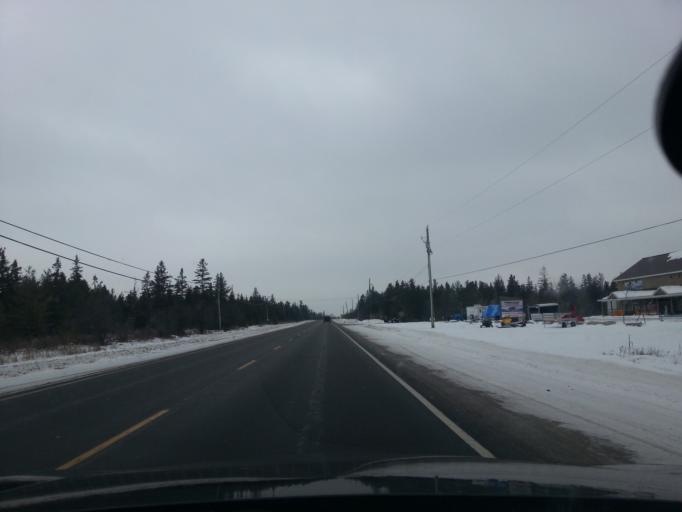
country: CA
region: Ontario
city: Carleton Place
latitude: 45.2495
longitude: -76.1605
